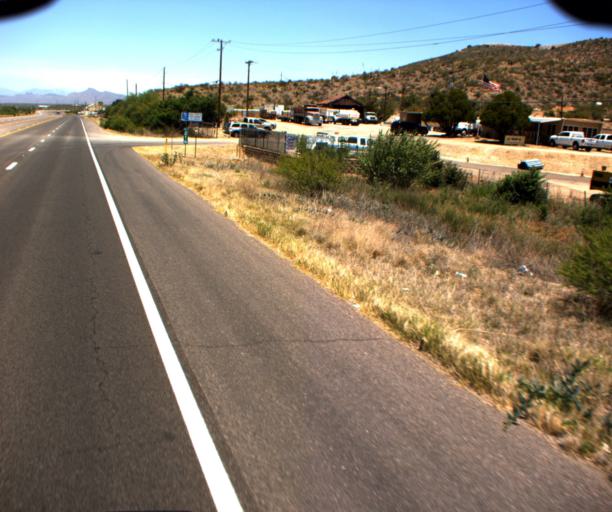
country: US
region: Arizona
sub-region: Gila County
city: Claypool
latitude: 33.4301
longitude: -110.8272
